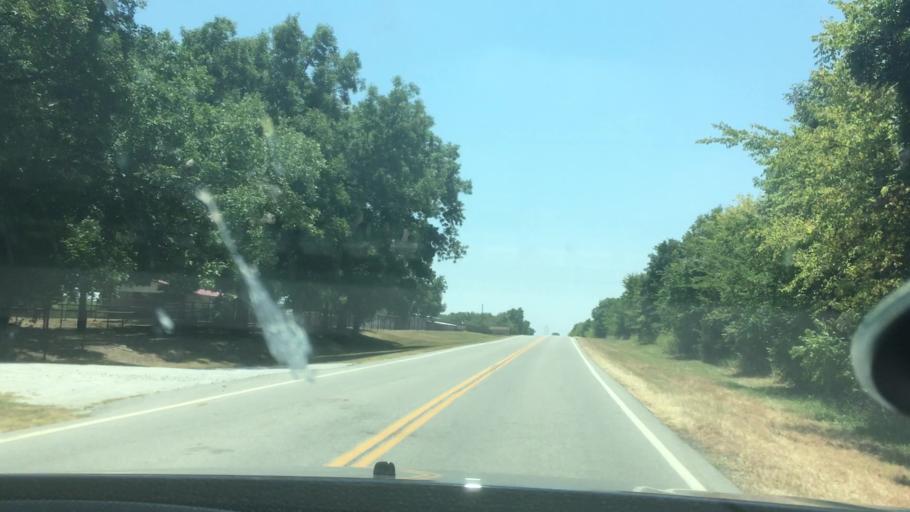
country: US
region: Oklahoma
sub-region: Coal County
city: Coalgate
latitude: 34.5326
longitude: -96.4070
